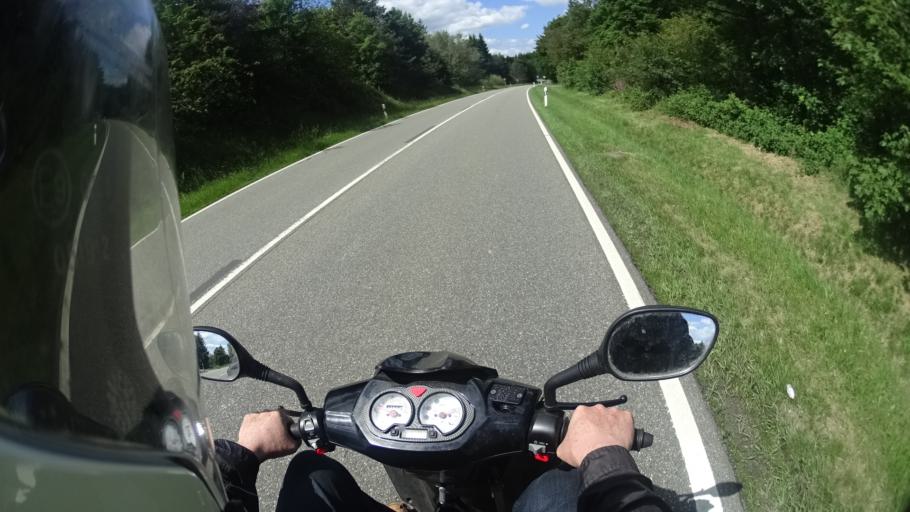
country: DE
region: Hesse
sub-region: Regierungsbezirk Darmstadt
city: Bad Schwalbach
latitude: 50.1381
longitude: 8.0445
